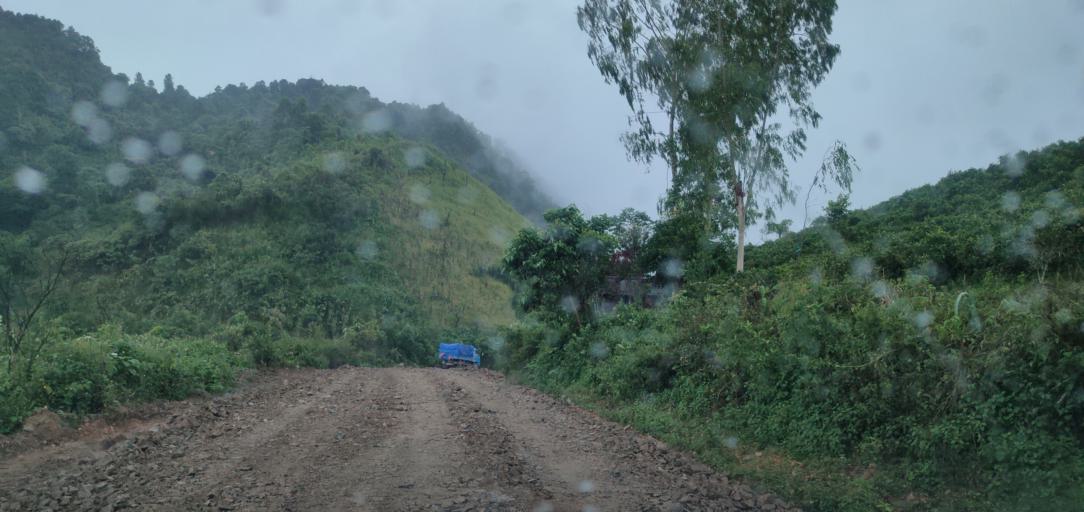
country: LA
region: Phongsali
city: Phongsali
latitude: 21.4309
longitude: 102.1606
